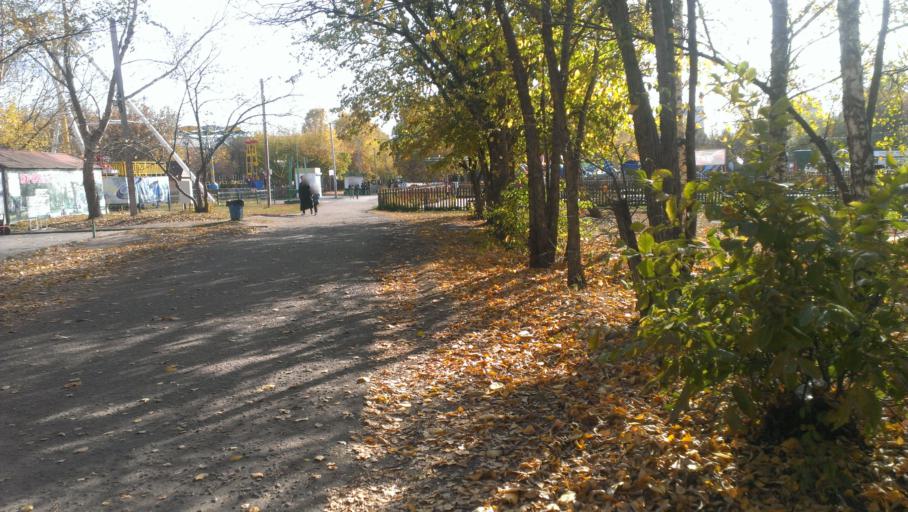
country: RU
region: Altai Krai
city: Novosilikatnyy
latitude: 53.3585
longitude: 83.6849
